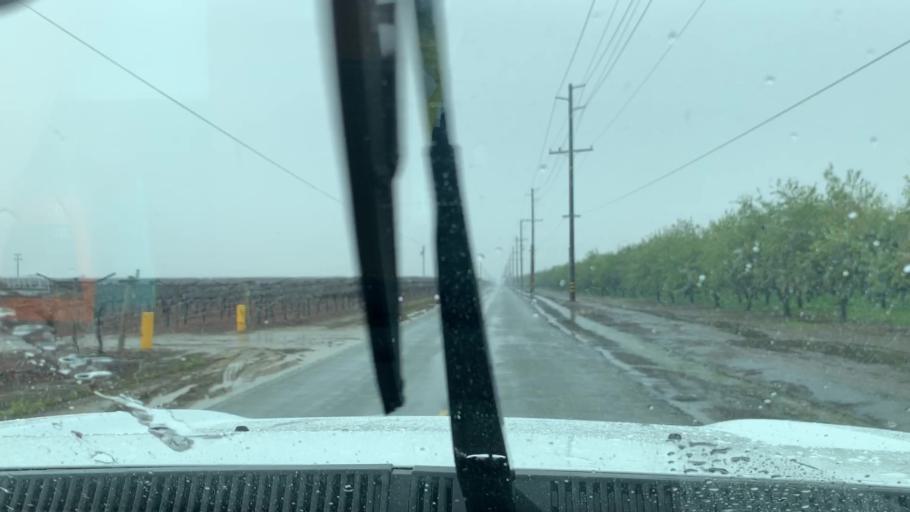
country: US
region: California
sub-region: Kern County
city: Delano
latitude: 35.8341
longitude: -119.1945
